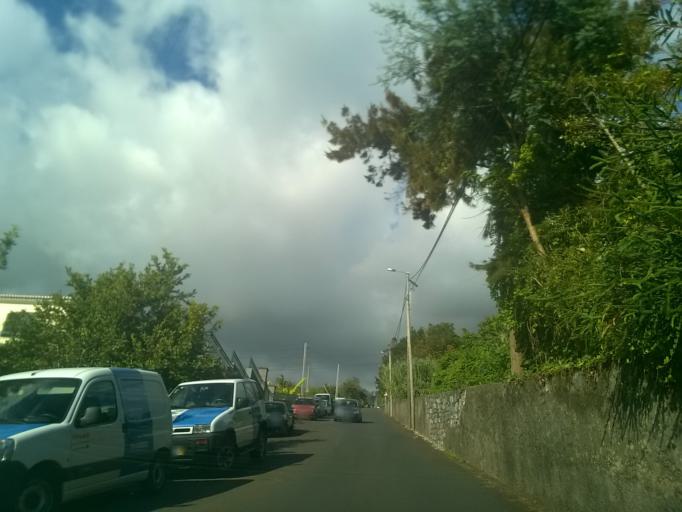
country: PT
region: Madeira
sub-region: Funchal
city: Nossa Senhora do Monte
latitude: 32.6688
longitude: -16.9055
